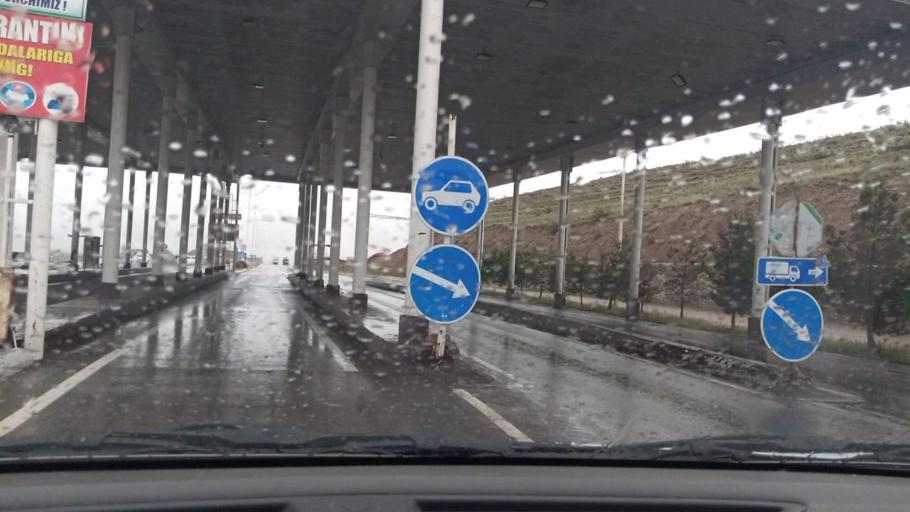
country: UZ
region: Namangan
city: Pop Shahri
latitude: 40.9225
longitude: 70.7339
